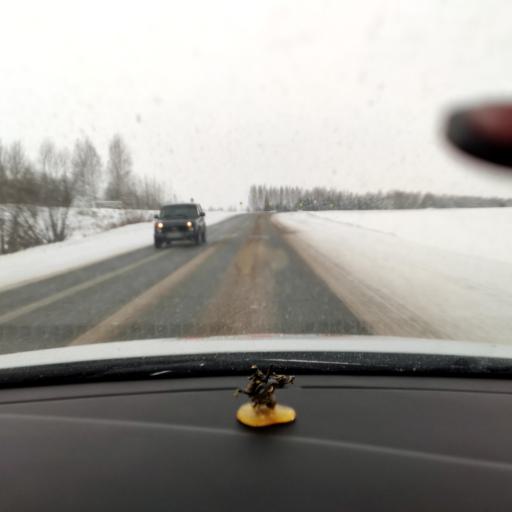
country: RU
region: Tatarstan
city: Vysokaya Gora
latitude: 56.0186
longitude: 49.2668
